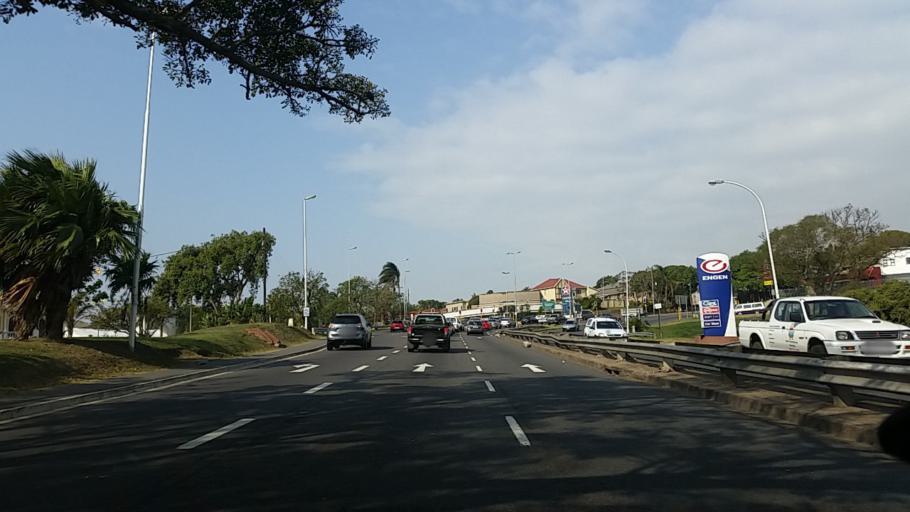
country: ZA
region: KwaZulu-Natal
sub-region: eThekwini Metropolitan Municipality
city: Berea
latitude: -29.8319
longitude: 30.9677
